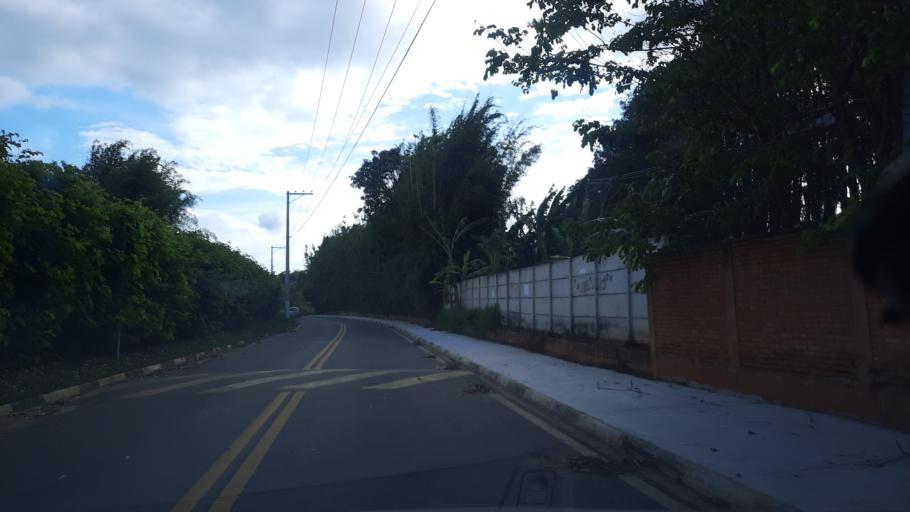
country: BR
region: Sao Paulo
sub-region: Atibaia
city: Atibaia
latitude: -23.0860
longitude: -46.5079
